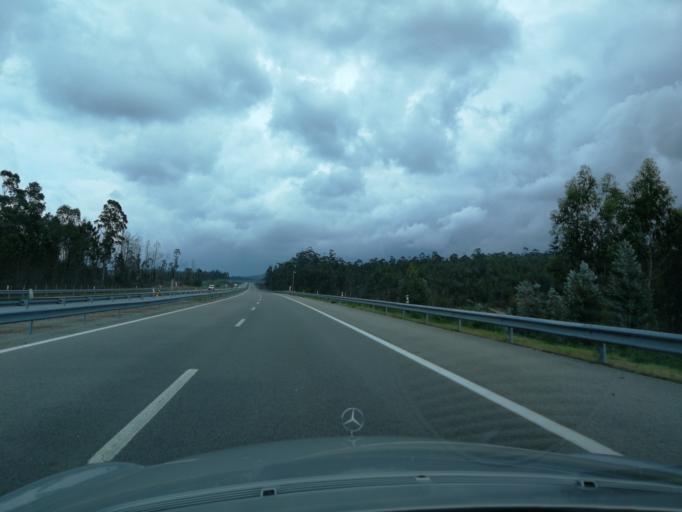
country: PT
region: Braga
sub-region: Vila Nova de Famalicao
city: Ribeirao
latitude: 41.3837
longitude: -8.6294
